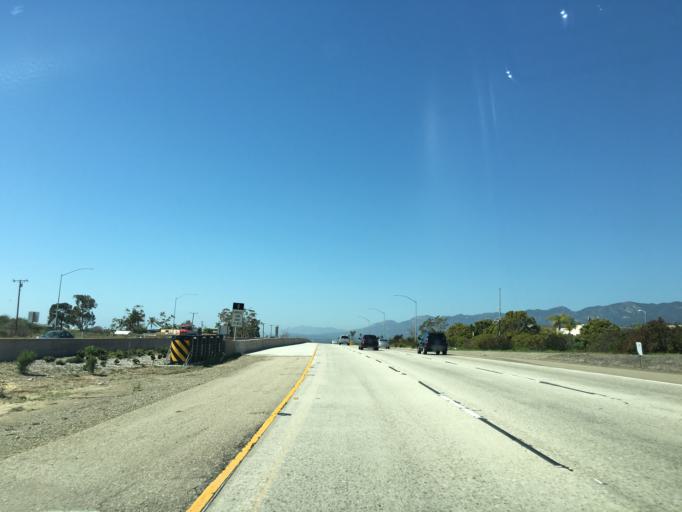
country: US
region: California
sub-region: Santa Barbara County
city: Carpinteria
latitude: 34.3846
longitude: -119.4860
